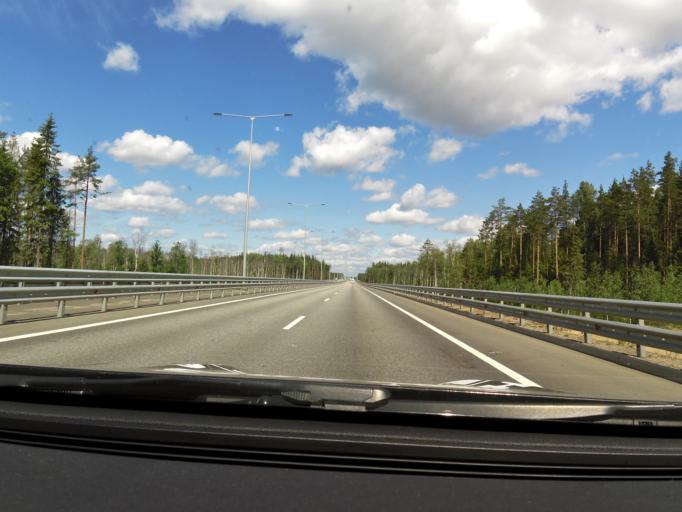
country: RU
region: Tverskaya
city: Krasnomayskiy
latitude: 57.6467
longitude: 34.2348
